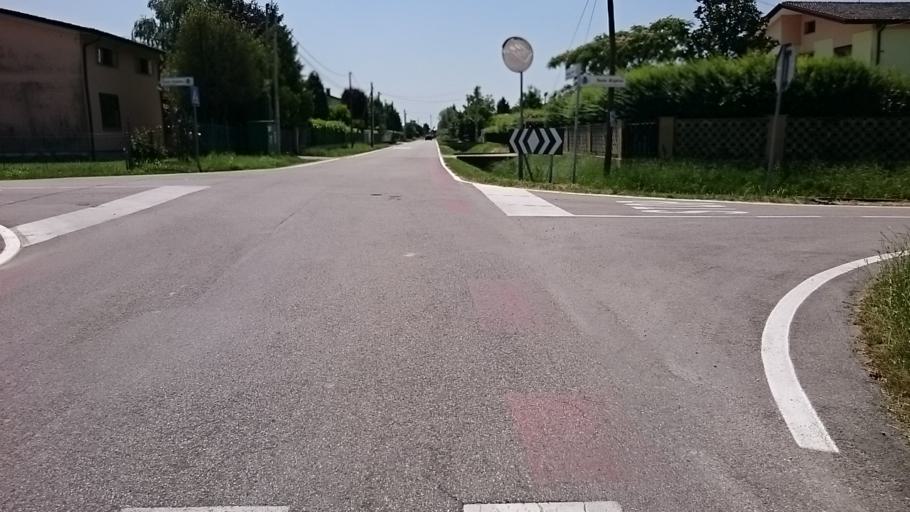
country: IT
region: Veneto
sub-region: Provincia di Padova
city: Villanova
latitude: 45.4953
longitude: 11.9796
